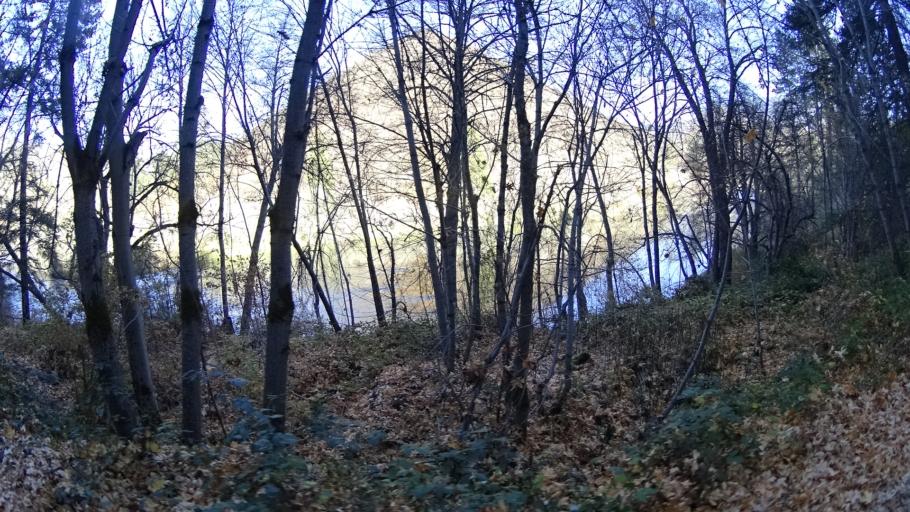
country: US
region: California
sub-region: Siskiyou County
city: Yreka
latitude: 41.8620
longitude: -122.7350
